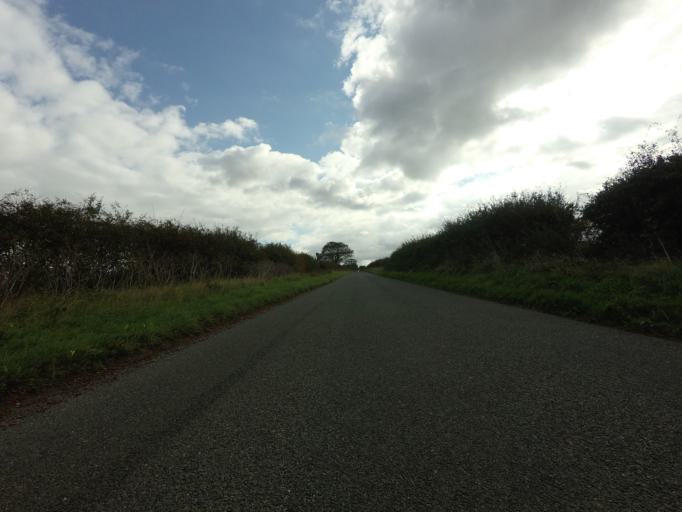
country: GB
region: England
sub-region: Norfolk
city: Hunstanton
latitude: 52.9250
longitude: 0.5399
